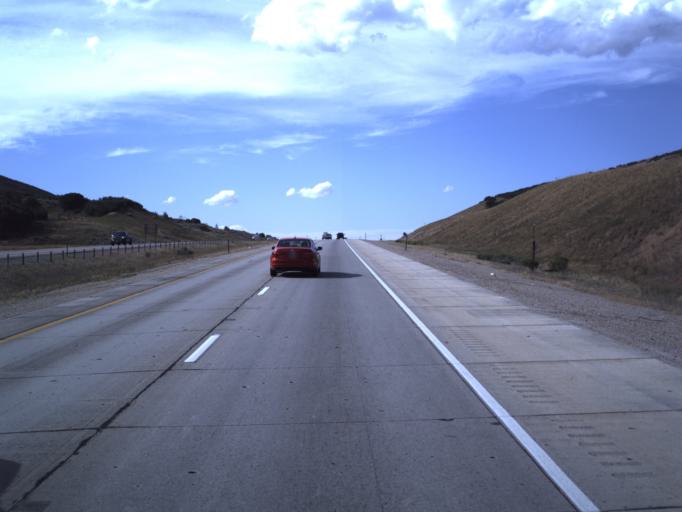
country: US
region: Utah
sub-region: Summit County
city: Park City
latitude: 40.6474
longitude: -111.4547
